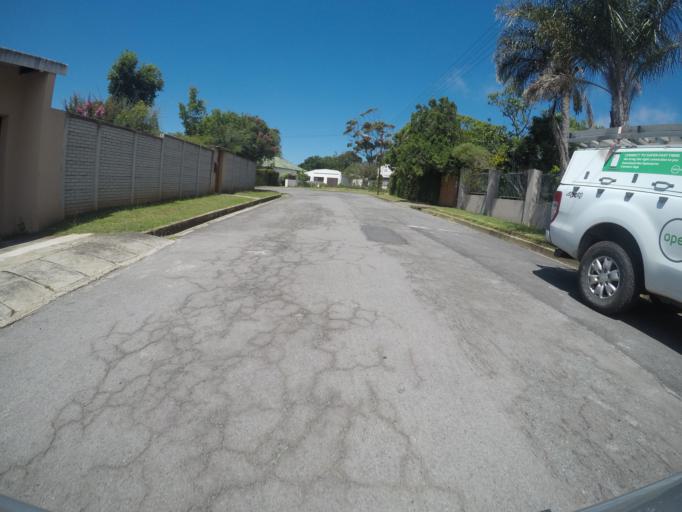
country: ZA
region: Eastern Cape
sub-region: Buffalo City Metropolitan Municipality
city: East London
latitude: -32.9745
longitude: 27.9046
